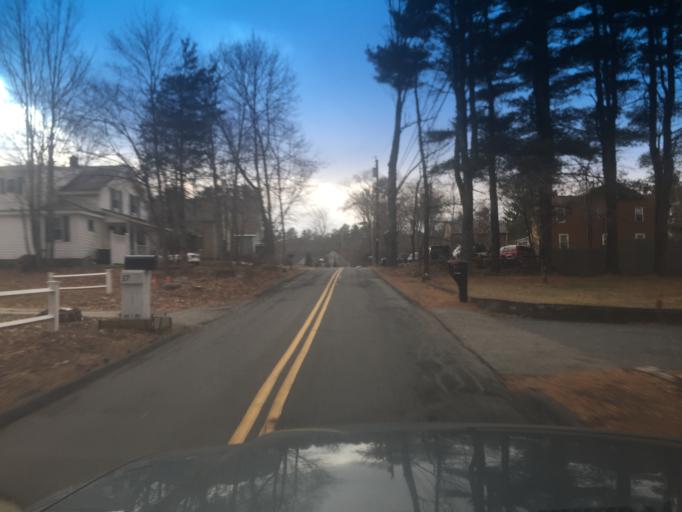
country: US
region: Massachusetts
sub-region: Norfolk County
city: Bellingham
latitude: 42.1163
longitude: -71.4478
